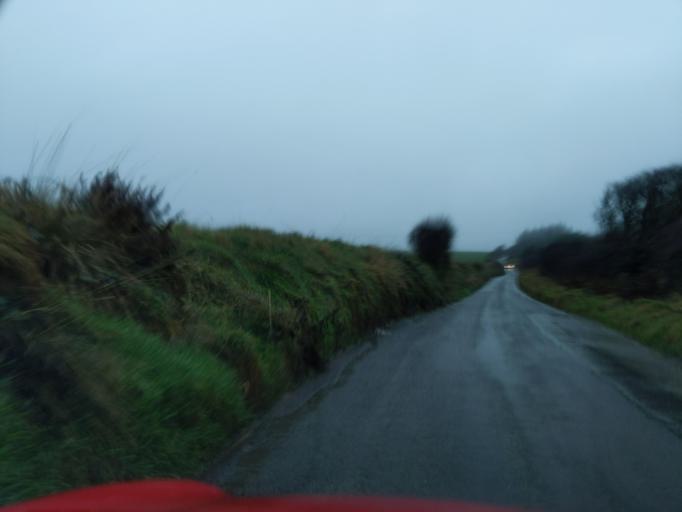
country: GB
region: England
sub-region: Cornwall
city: Camelford
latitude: 50.6468
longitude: -4.6990
